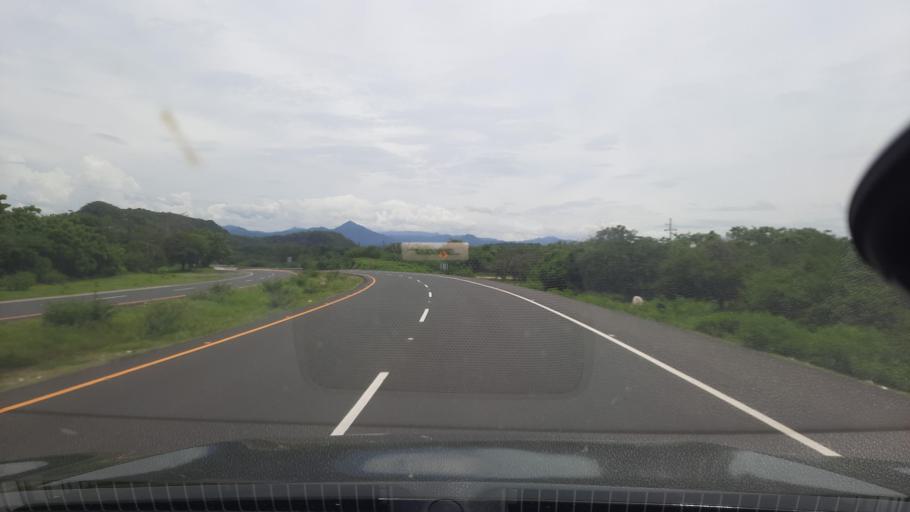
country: HN
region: Valle
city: Aramecina
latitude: 13.7146
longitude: -87.7063
